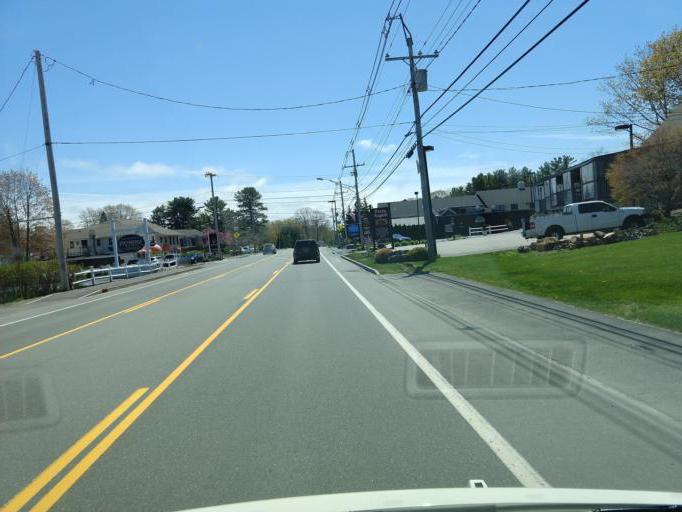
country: US
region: Maine
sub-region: York County
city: Ogunquit
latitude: 43.2649
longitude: -70.5978
